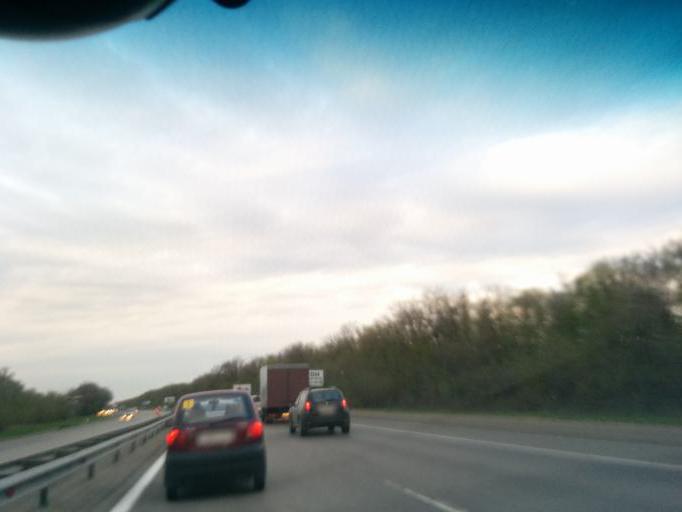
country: RU
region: Rostov
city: Grushevskaya
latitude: 47.3996
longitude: 39.9567
